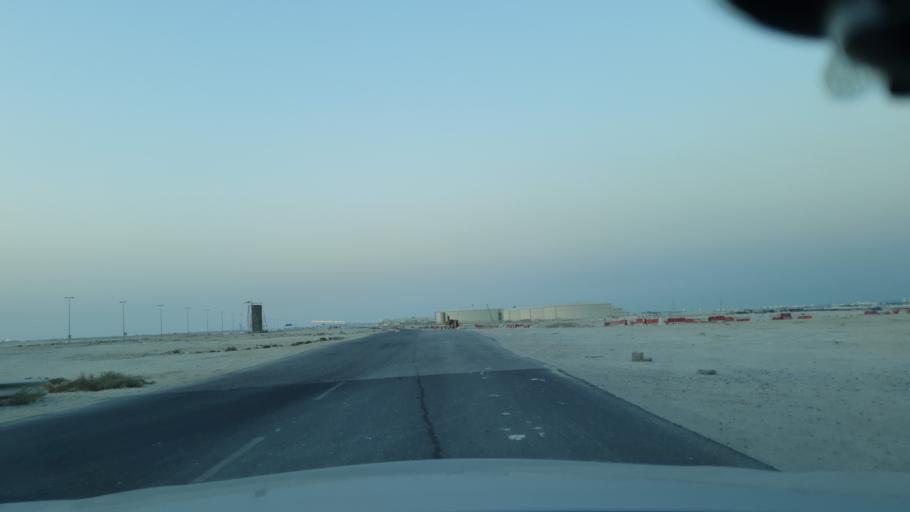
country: BH
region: Central Governorate
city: Dar Kulayb
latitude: 25.9698
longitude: 50.6017
